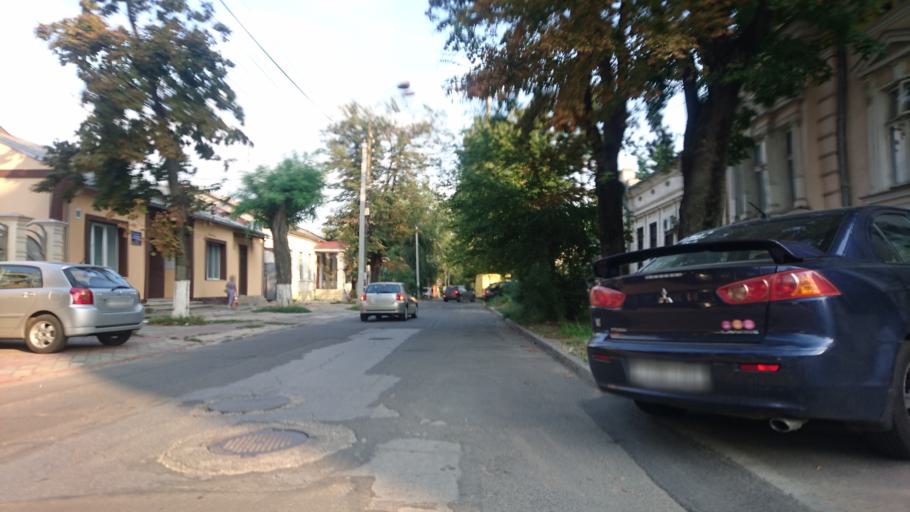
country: MD
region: Chisinau
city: Chisinau
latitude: 47.0297
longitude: 28.8190
